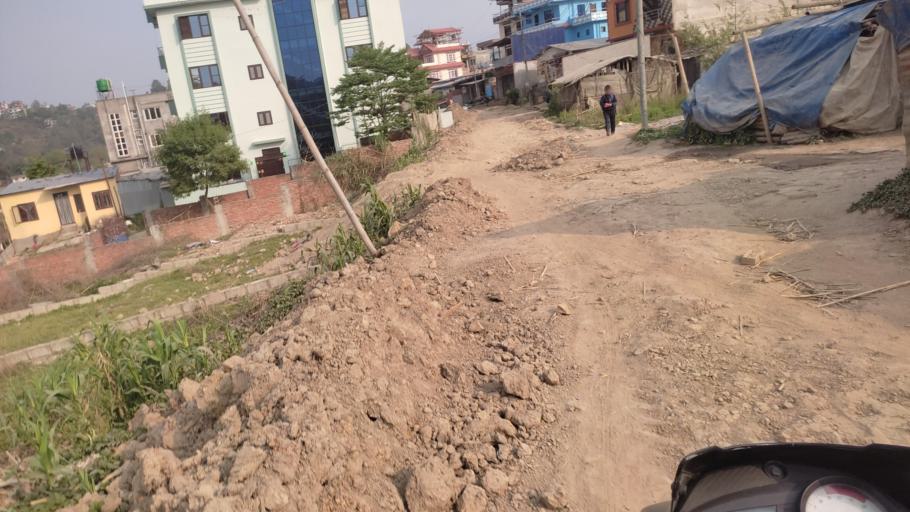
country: NP
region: Central Region
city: Kirtipur
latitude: 27.6596
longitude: 85.2877
